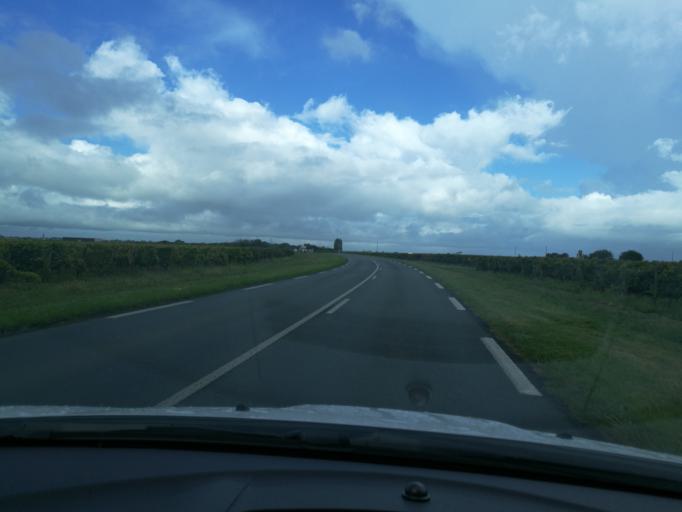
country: FR
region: Poitou-Charentes
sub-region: Departement de la Charente-Maritime
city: Le Bois-Plage-en-Re
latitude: 46.2000
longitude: -1.3910
